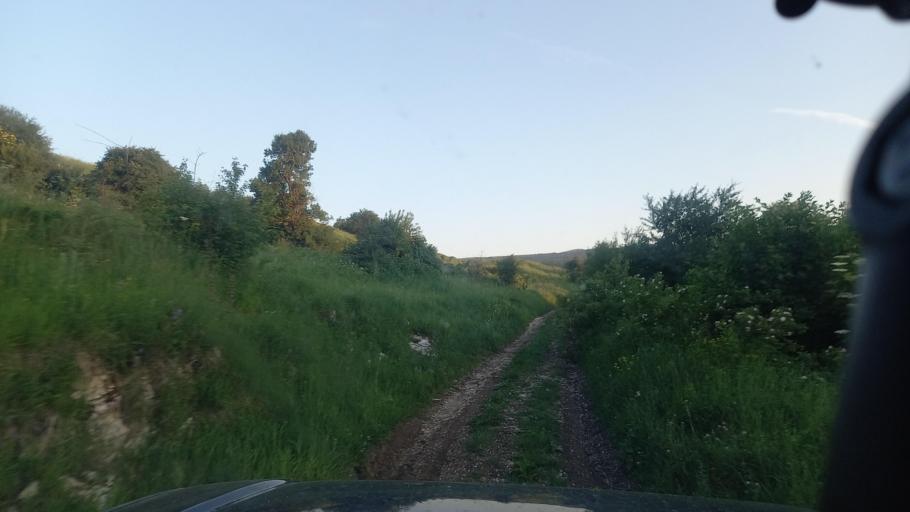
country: RU
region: Karachayevo-Cherkesiya
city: Pregradnaya
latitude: 44.1068
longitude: 41.1287
